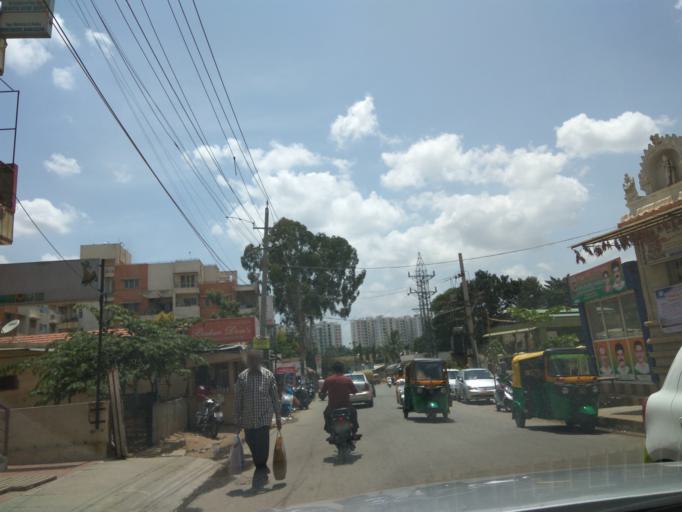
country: IN
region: Karnataka
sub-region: Bangalore Urban
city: Bangalore
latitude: 12.9857
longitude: 77.6718
